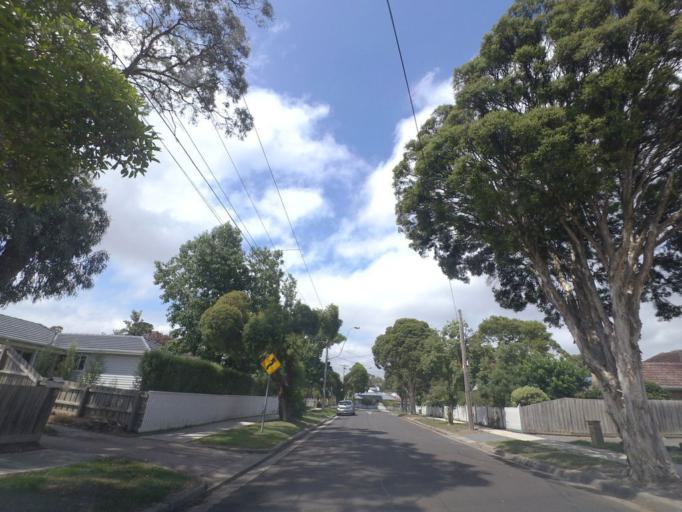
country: AU
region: Victoria
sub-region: Maroondah
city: Heathmont
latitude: -37.8300
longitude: 145.2318
